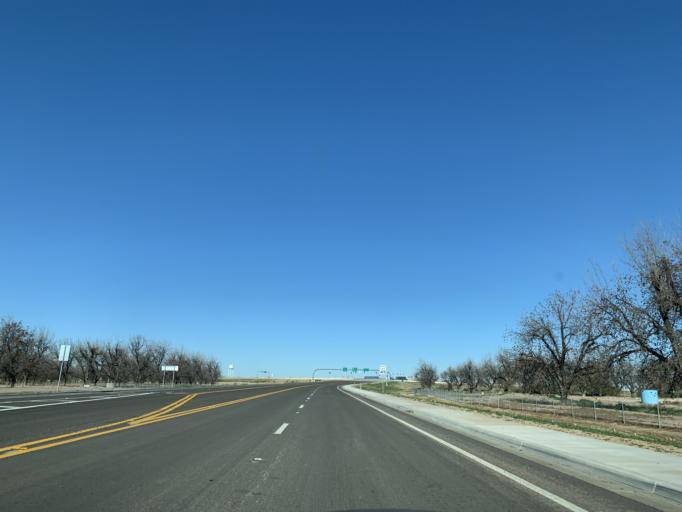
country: US
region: Arizona
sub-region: Pinal County
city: Eloy
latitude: 32.7200
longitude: -111.5175
